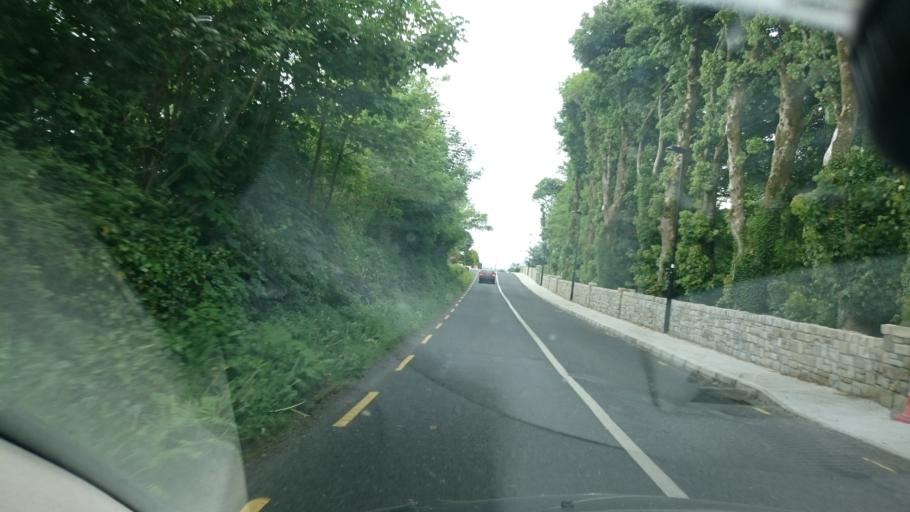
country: IE
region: Connaught
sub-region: Sligo
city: Inishcrone
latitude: 54.1091
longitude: -9.0308
